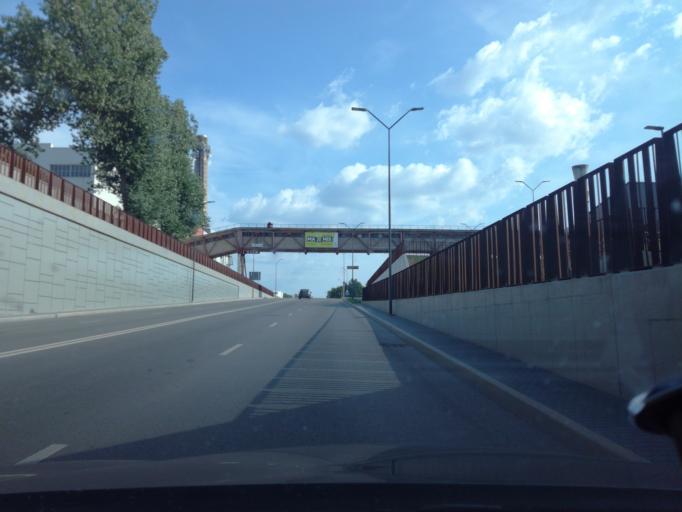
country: LT
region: Marijampoles apskritis
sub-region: Marijampole Municipality
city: Marijampole
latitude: 54.5378
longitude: 23.3510
